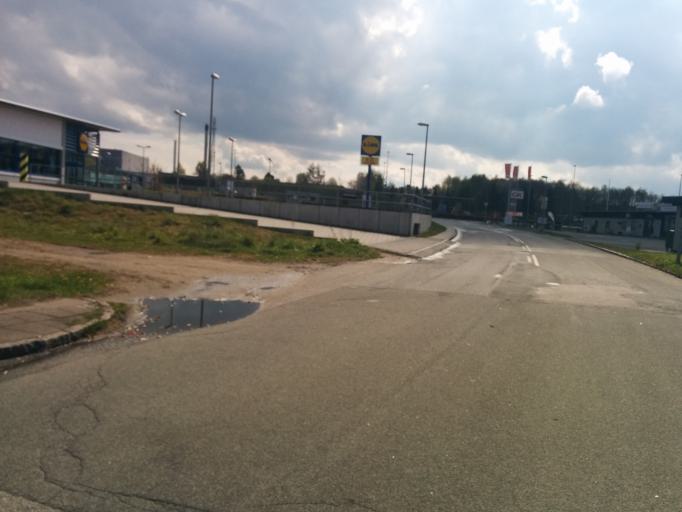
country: DK
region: Central Jutland
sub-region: Viborg Kommune
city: Viborg
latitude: 56.4454
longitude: 9.3910
